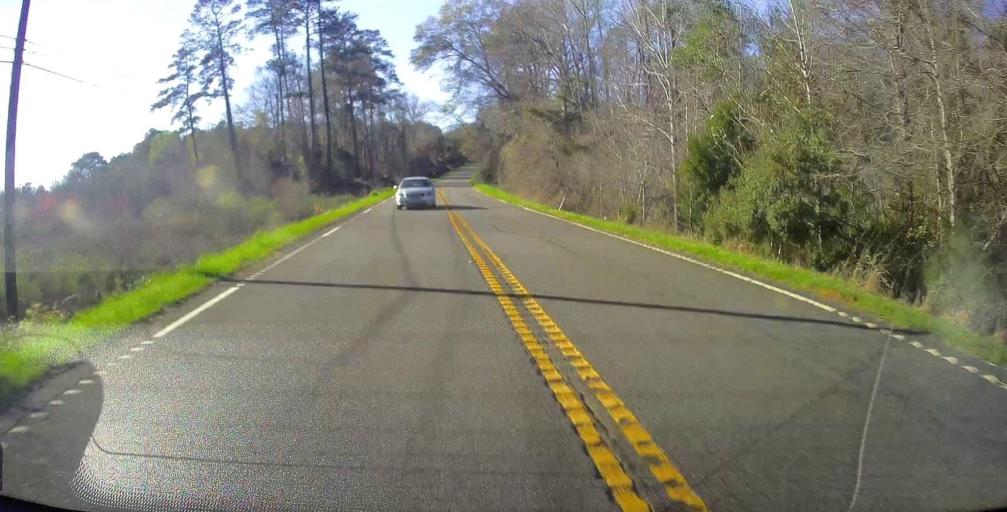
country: US
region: Georgia
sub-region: Macon County
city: Marshallville
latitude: 32.4487
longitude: -83.9074
